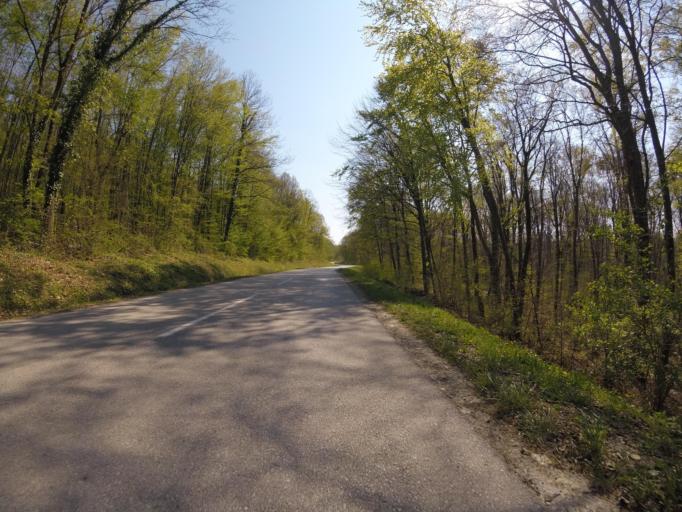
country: HR
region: Zagrebacka
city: Lukavec
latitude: 45.6351
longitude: 15.9624
